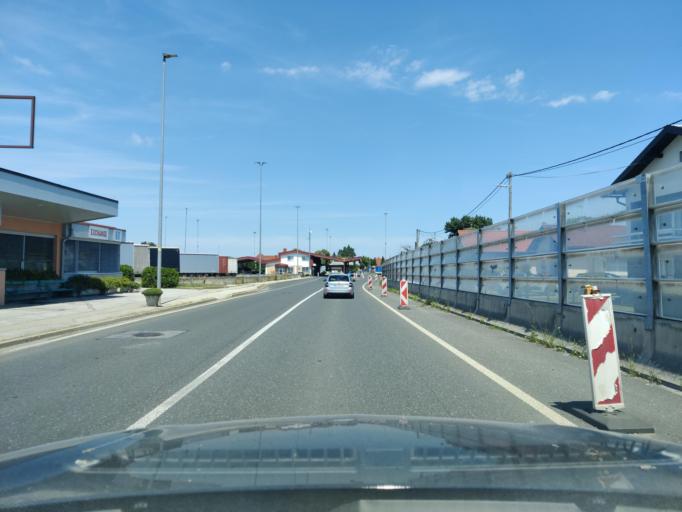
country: SI
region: Lendava-Lendva
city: Lendava
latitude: 46.5950
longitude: 16.4603
